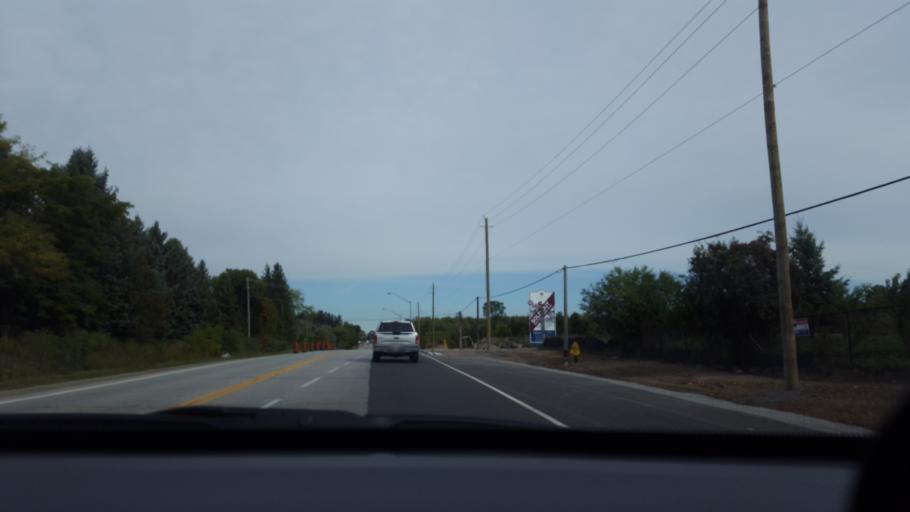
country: CA
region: Ontario
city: Vaughan
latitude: 43.9416
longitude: -79.5317
